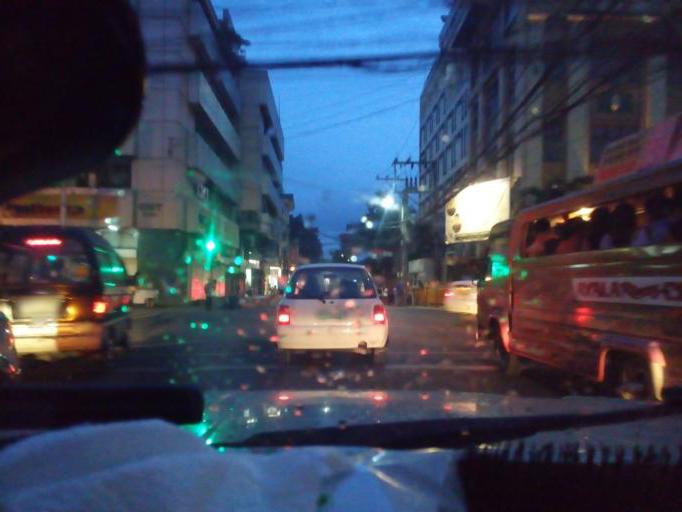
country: PH
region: Central Visayas
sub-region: Cebu City
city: Calero
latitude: 10.3008
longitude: 123.8987
